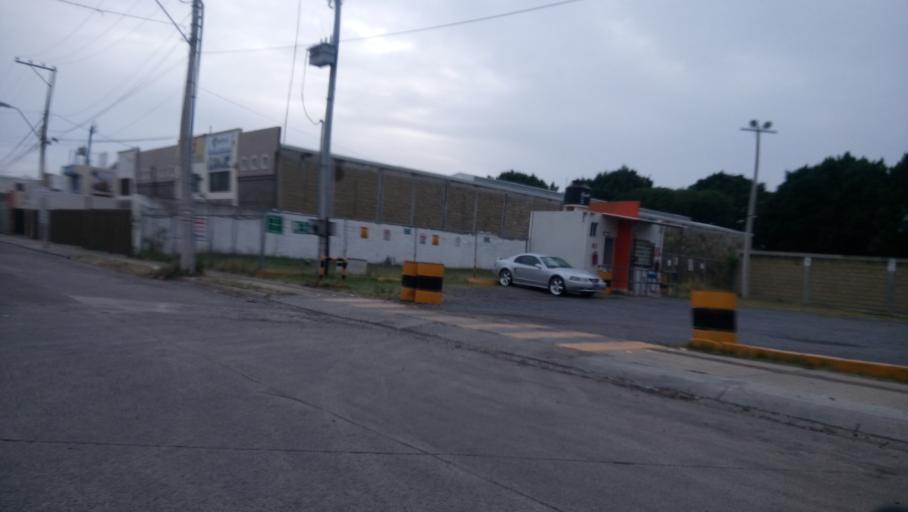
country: MX
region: Guanajuato
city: Leon
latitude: 21.1448
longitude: -101.6621
